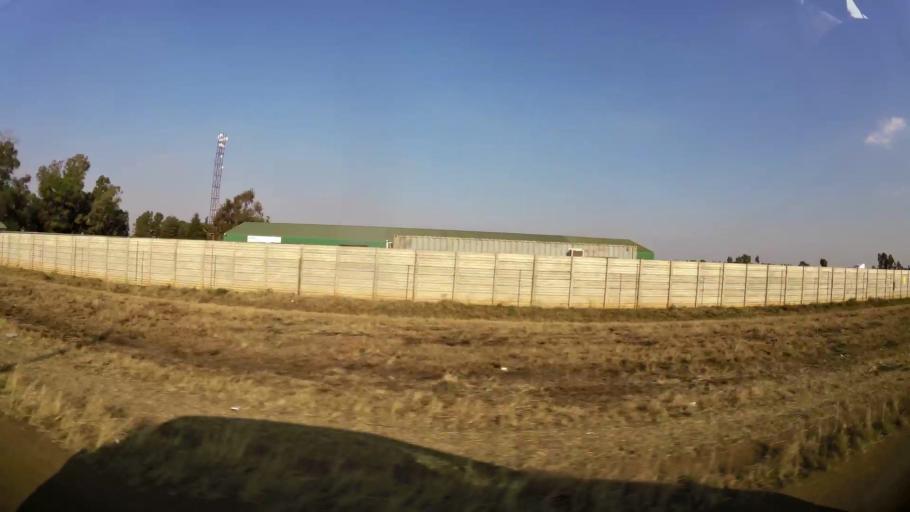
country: ZA
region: Gauteng
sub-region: Ekurhuleni Metropolitan Municipality
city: Benoni
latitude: -26.1046
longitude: 28.3789
